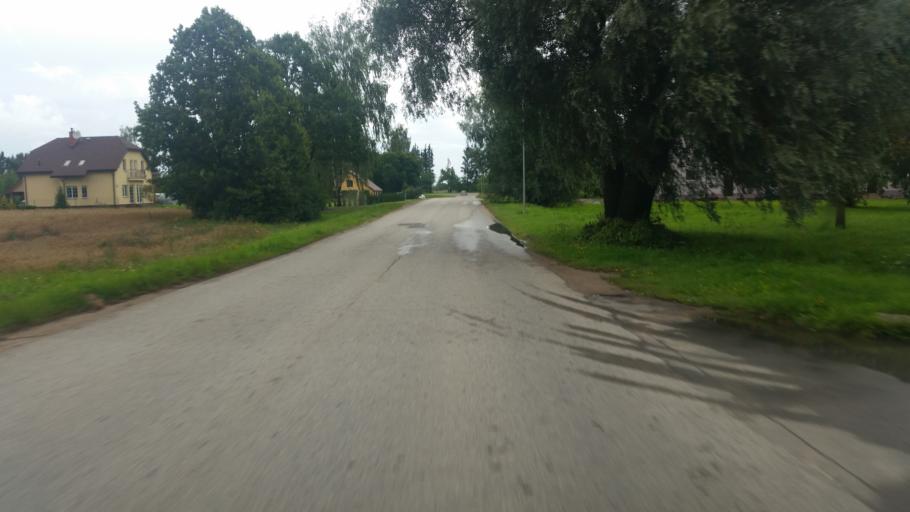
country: LV
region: Bauskas Rajons
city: Bauska
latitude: 56.4173
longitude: 24.1935
